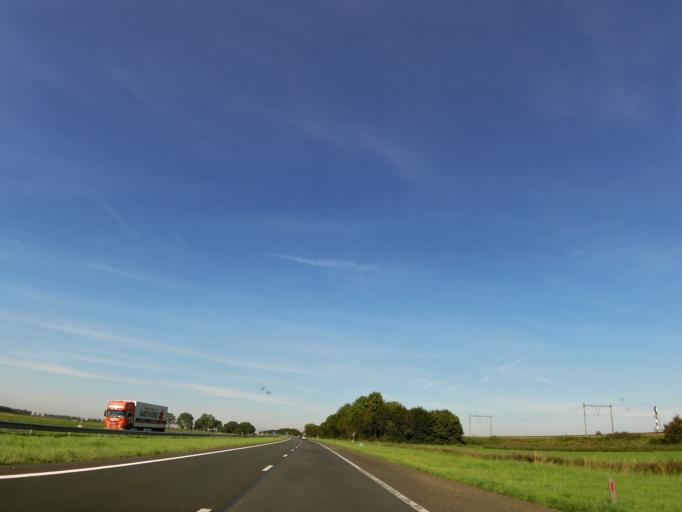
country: NL
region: Zeeland
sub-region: Gemeente Noord-Beveland
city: Kamperland
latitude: 51.5016
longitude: 3.7308
